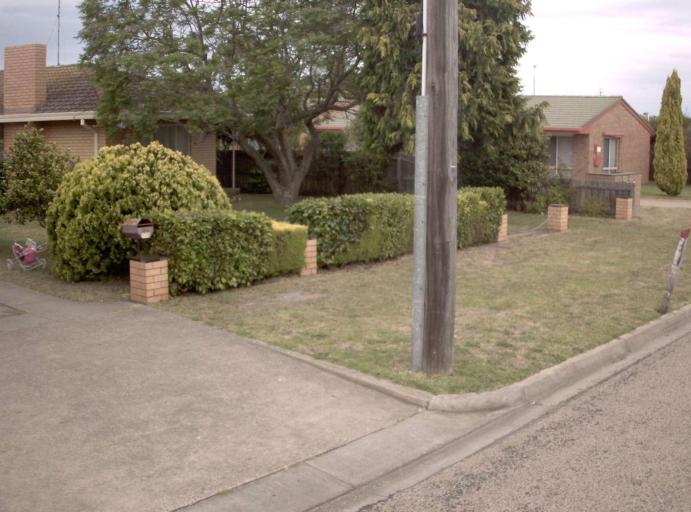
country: AU
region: Victoria
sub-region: East Gippsland
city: Bairnsdale
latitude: -37.9094
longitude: 147.7204
